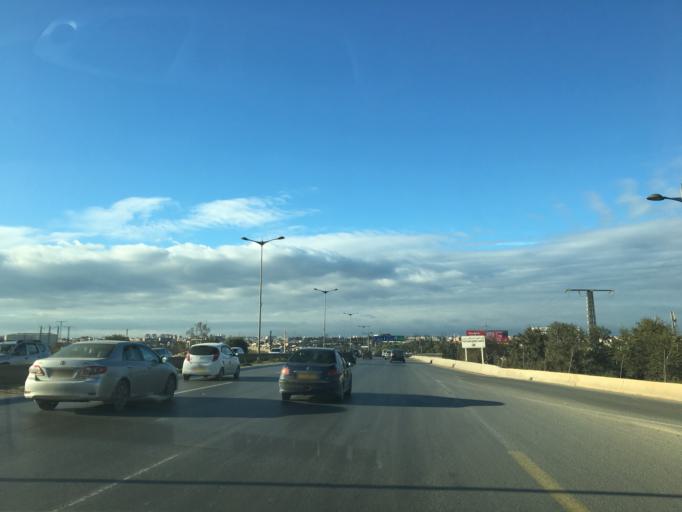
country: DZ
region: Tipaza
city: Baraki
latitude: 36.6999
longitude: 3.1194
